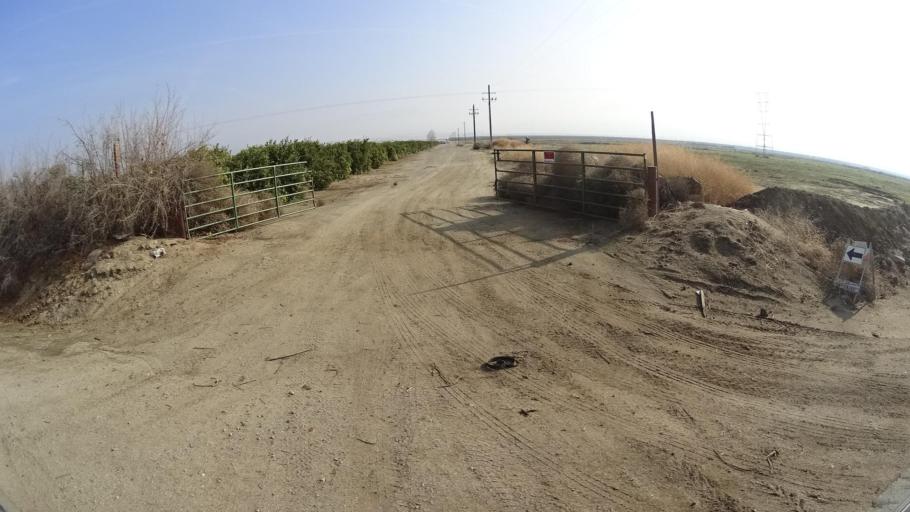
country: US
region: California
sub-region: Kern County
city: Lebec
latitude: 35.0235
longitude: -118.8466
